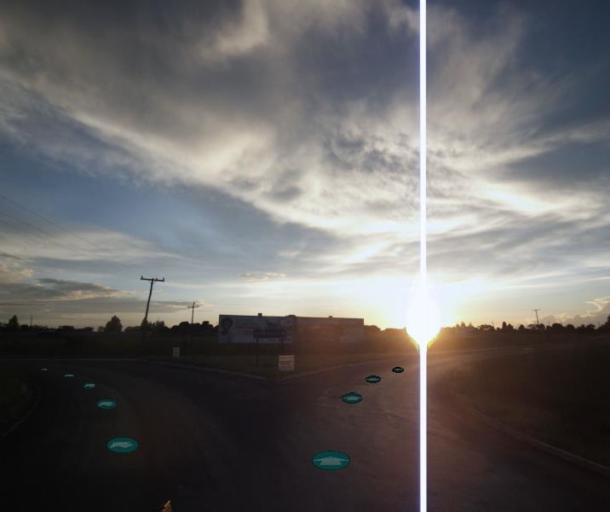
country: BR
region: Goias
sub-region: Abadiania
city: Abadiania
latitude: -16.0519
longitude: -48.8534
